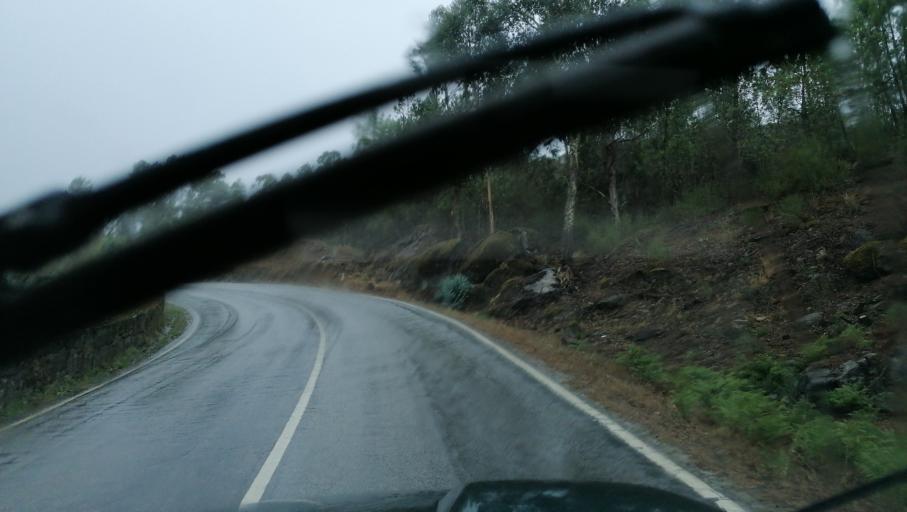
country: PT
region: Braga
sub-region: Cabeceiras de Basto
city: Cabeceiras de Basto
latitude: 41.4985
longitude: -7.9003
